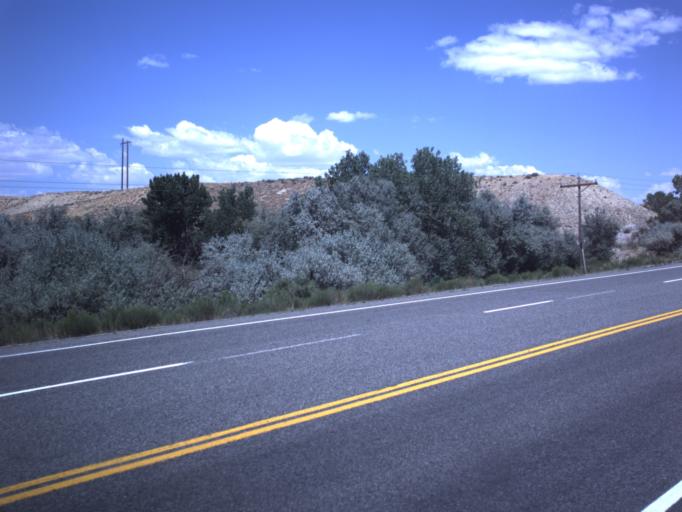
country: US
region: Utah
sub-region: Emery County
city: Huntington
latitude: 39.3391
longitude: -110.9493
